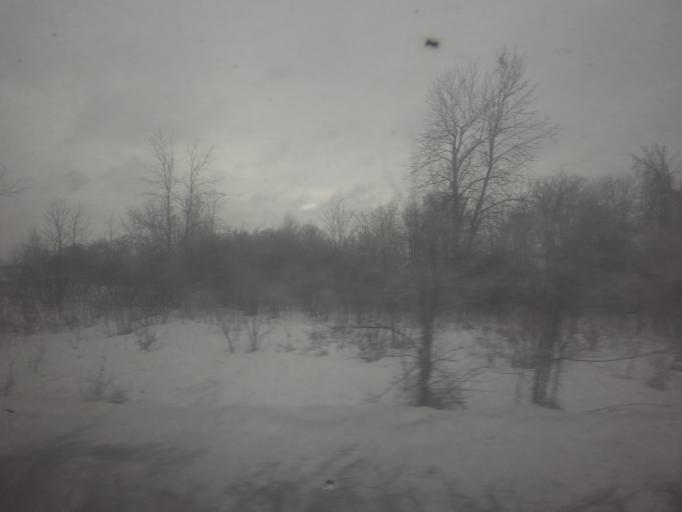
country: CA
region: Ontario
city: Bells Corners
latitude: 45.2043
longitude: -75.8126
